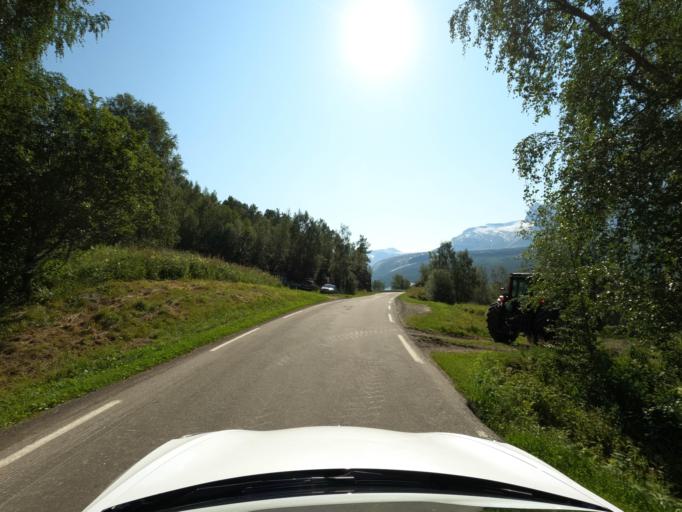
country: NO
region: Nordland
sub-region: Narvik
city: Narvik
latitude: 68.2937
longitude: 17.3571
